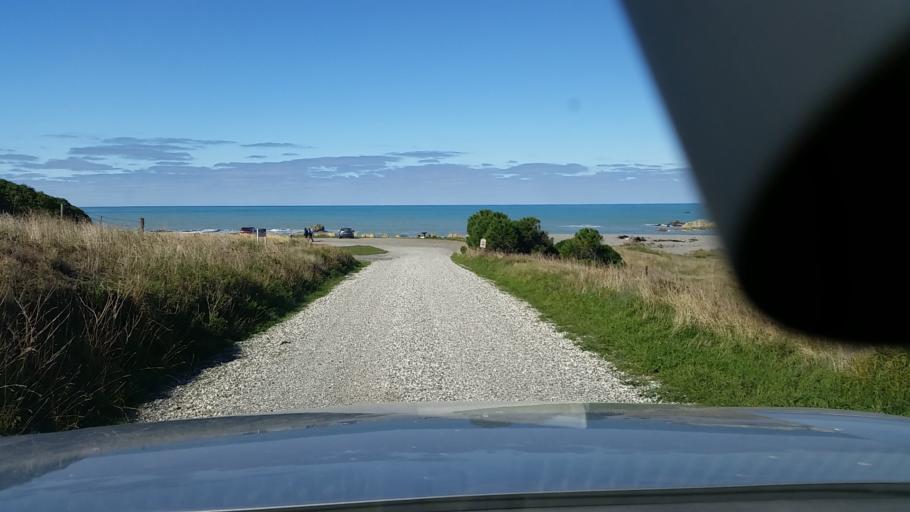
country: NZ
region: Marlborough
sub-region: Marlborough District
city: Blenheim
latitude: -41.8441
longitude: 174.1826
